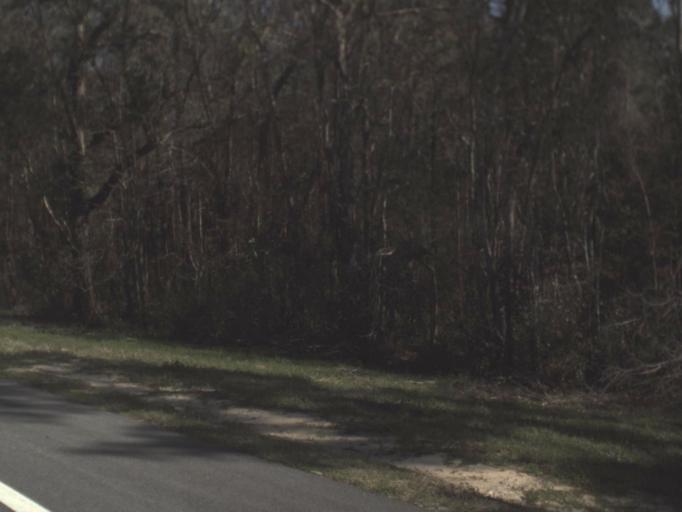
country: US
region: Florida
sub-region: Jefferson County
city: Monticello
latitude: 30.4909
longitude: -84.0260
